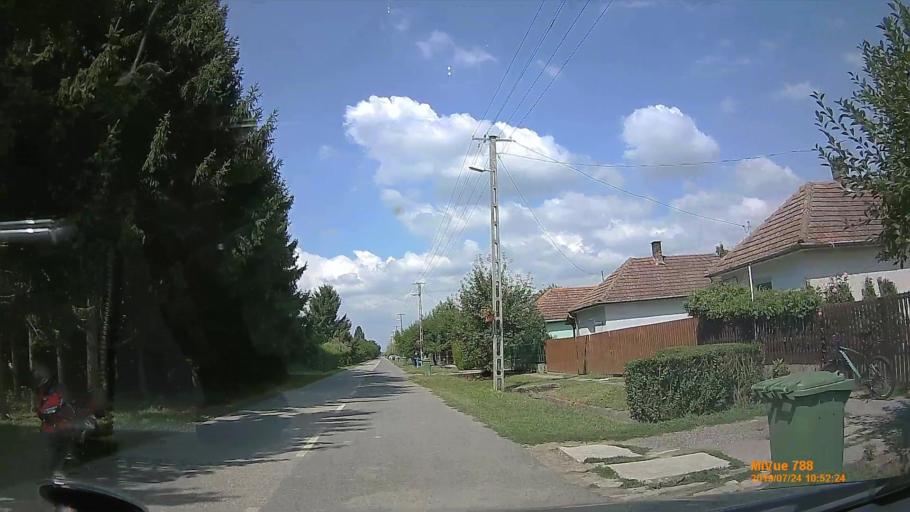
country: UA
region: Zakarpattia
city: Berehove
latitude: 48.1970
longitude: 22.5547
